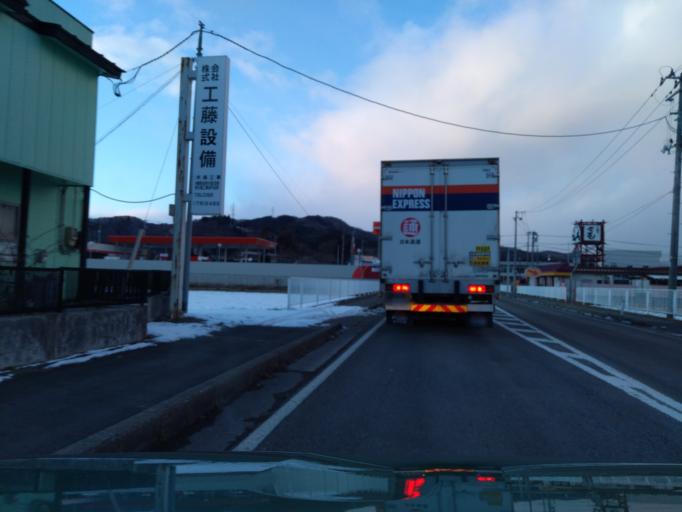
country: JP
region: Iwate
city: Shizukuishi
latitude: 39.6990
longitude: 141.0627
